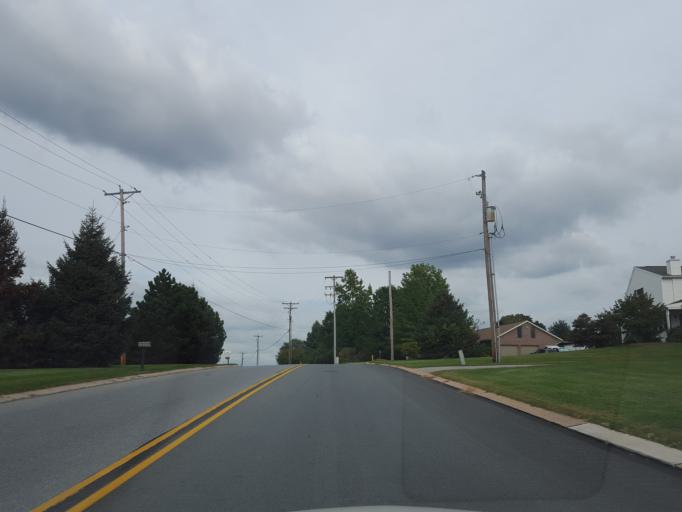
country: US
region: Pennsylvania
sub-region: York County
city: Yoe
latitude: 39.9426
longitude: -76.6513
